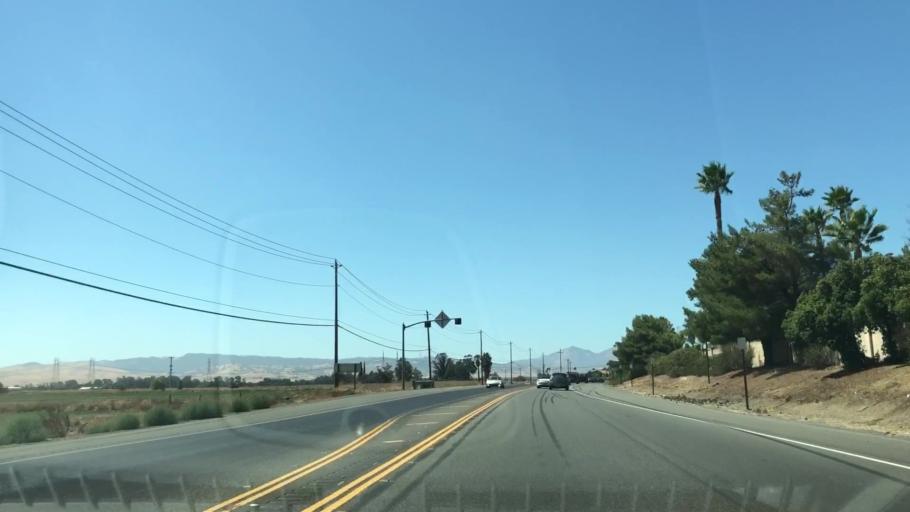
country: US
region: California
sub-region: Contra Costa County
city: Discovery Bay
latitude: 37.8901
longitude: -121.6038
